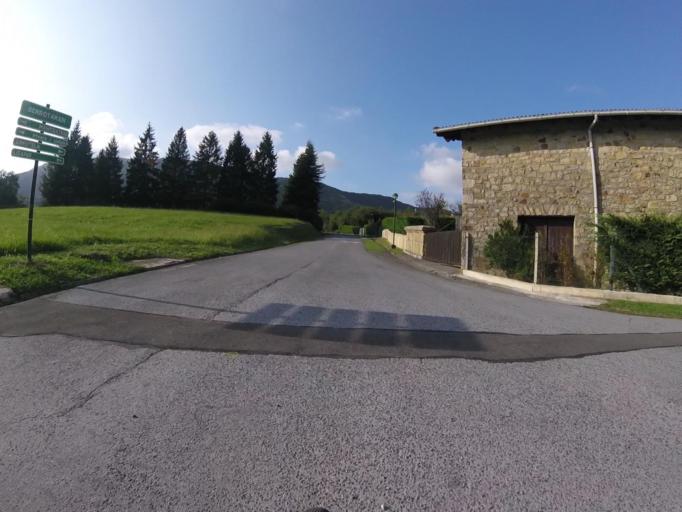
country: ES
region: Basque Country
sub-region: Provincia de Guipuzcoa
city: Irun
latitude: 43.3386
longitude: -1.8347
